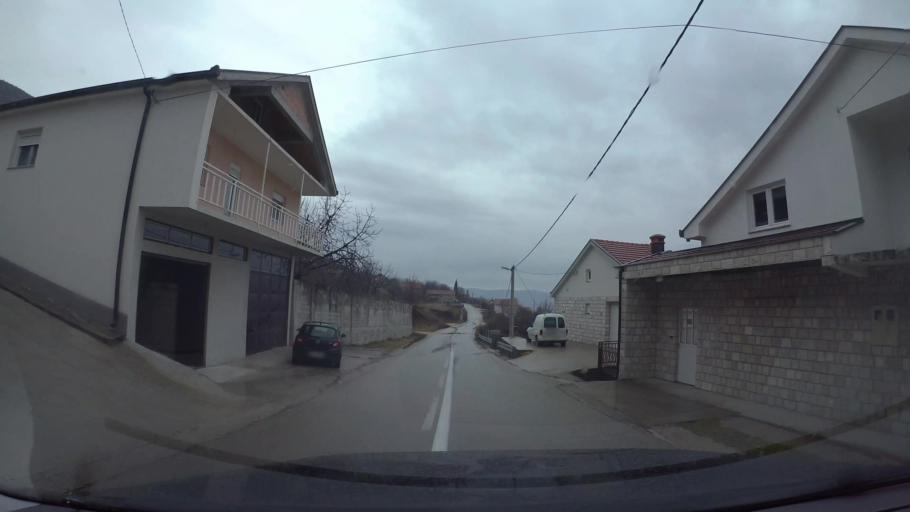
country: BA
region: Federation of Bosnia and Herzegovina
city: Rodoc
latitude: 43.3019
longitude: 17.8538
